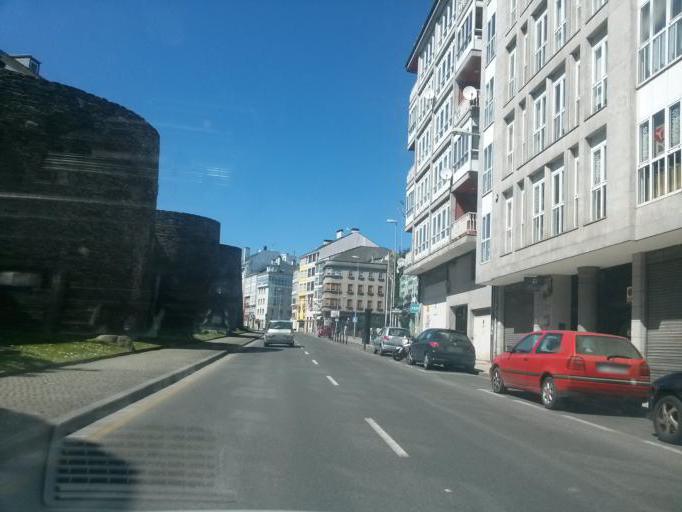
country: ES
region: Galicia
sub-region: Provincia de Lugo
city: Lugo
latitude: 43.0136
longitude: -7.5557
